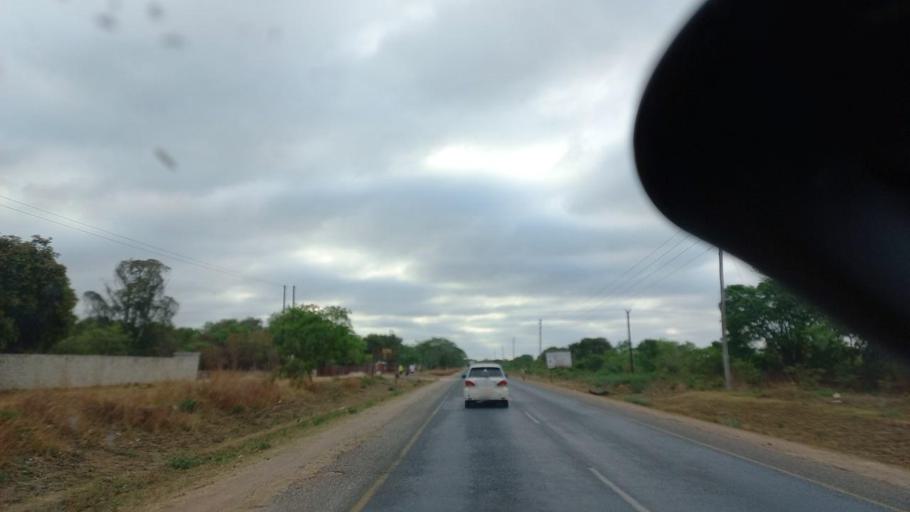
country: ZM
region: Lusaka
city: Chongwe
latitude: -15.3495
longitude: 28.5346
